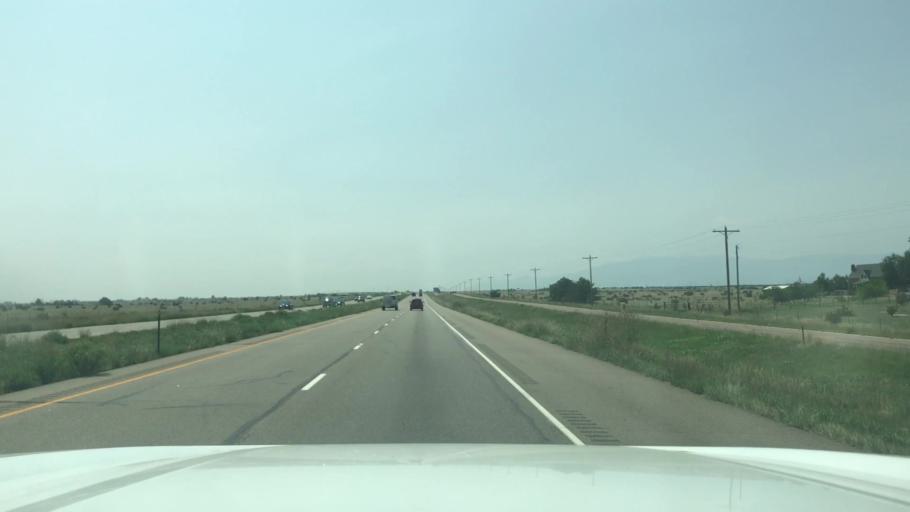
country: US
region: Colorado
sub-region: Pueblo County
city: Pueblo
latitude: 38.0909
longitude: -104.6949
